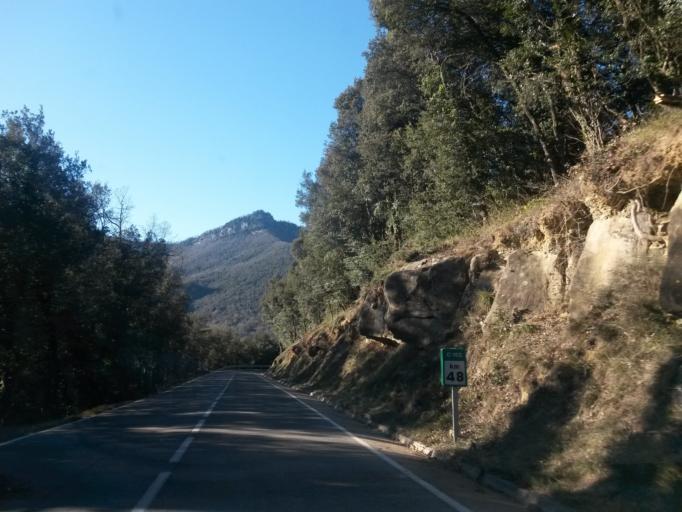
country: ES
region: Catalonia
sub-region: Provincia de Girona
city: Bas
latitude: 42.0938
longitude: 2.4648
